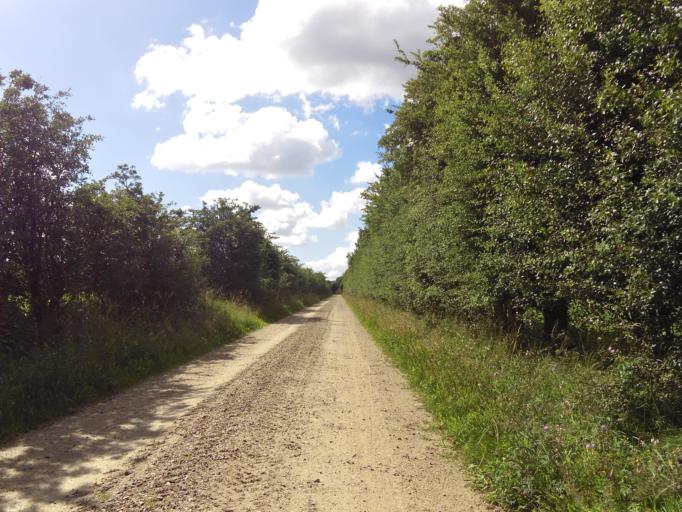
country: DK
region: South Denmark
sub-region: Vejen Kommune
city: Rodding
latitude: 55.3283
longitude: 9.1854
